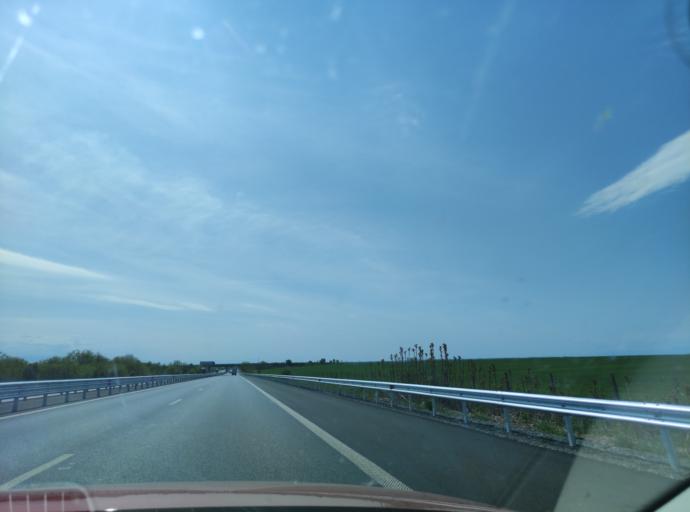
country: BG
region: Stara Zagora
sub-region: Obshtina Chirpan
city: Chirpan
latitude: 42.1949
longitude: 25.2404
